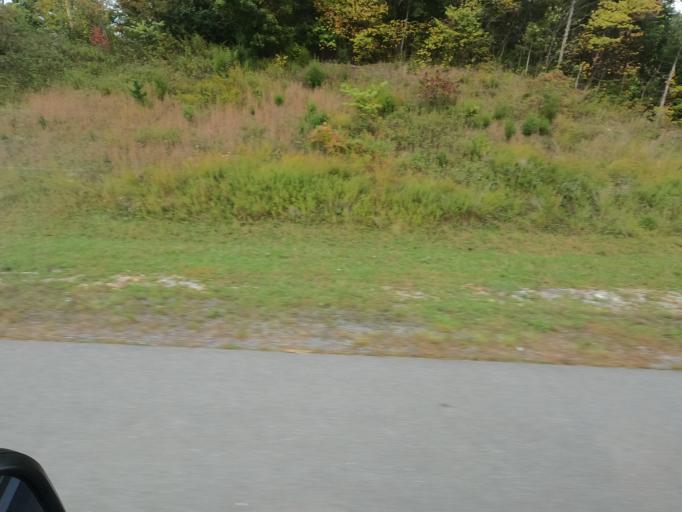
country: US
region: Tennessee
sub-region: Carter County
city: Central
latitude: 36.2843
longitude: -82.2435
